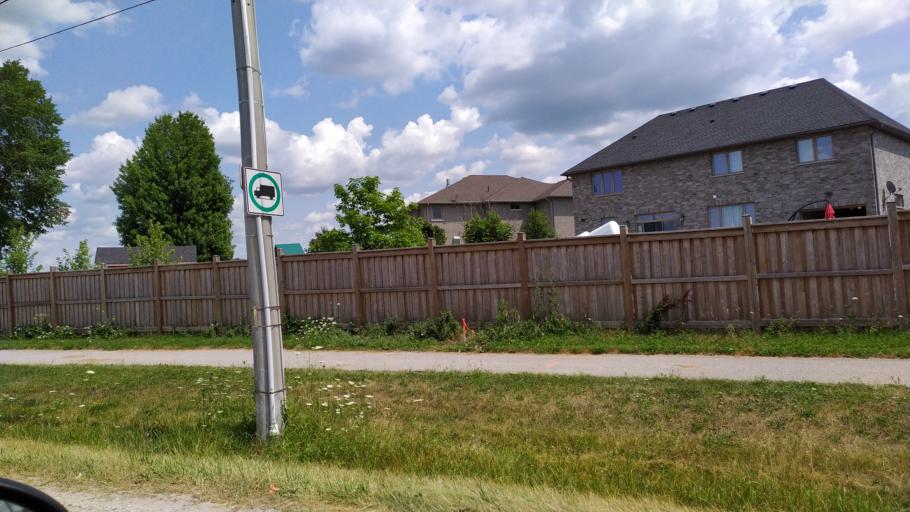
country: CA
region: Ontario
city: Stratford
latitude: 43.3732
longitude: -81.0107
